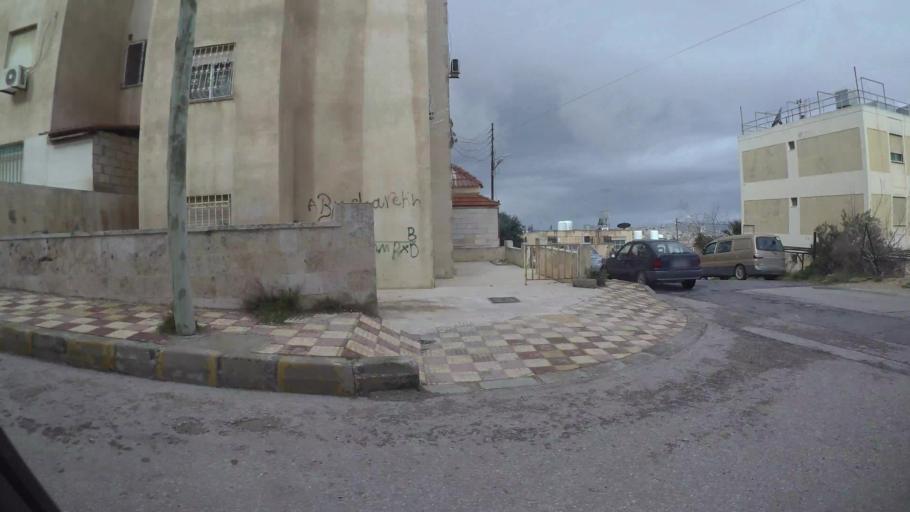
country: JO
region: Amman
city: Al Jubayhah
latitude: 32.0578
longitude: 35.8877
